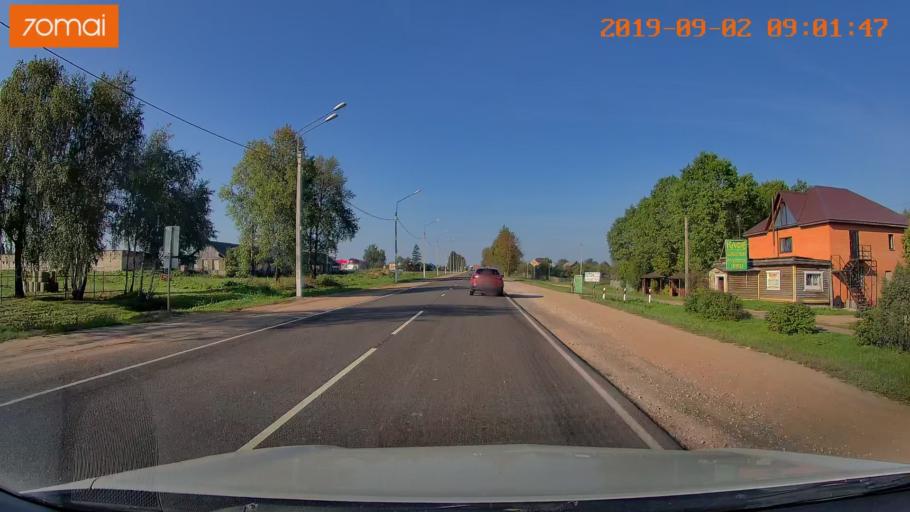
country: RU
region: Kaluga
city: Myatlevo
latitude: 54.9040
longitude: 35.6817
